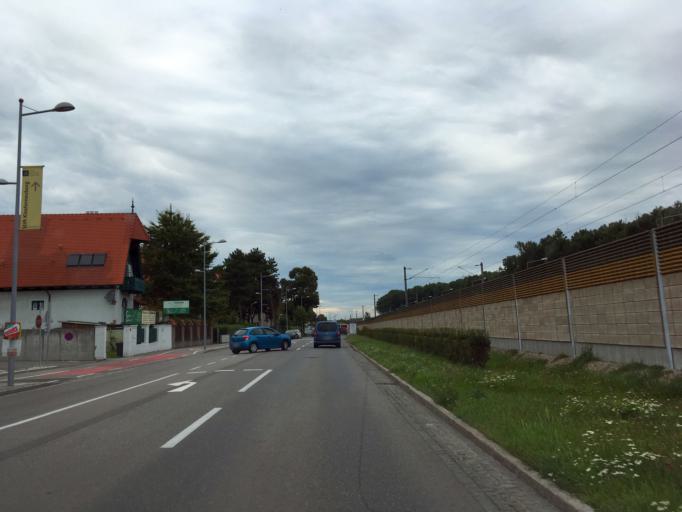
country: AT
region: Lower Austria
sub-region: Politischer Bezirk Wien-Umgebung
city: Klosterneuburg
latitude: 48.3031
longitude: 16.3310
